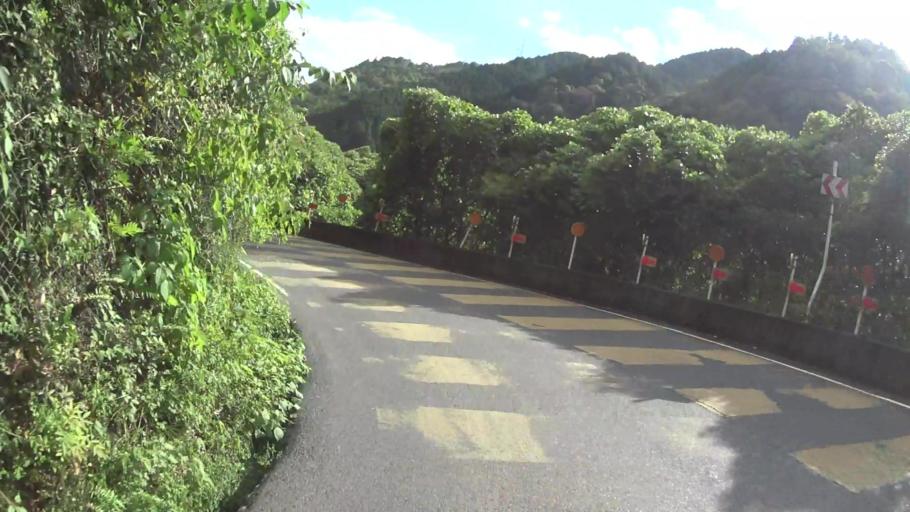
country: JP
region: Kyoto
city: Uji
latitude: 34.9031
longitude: 135.8676
